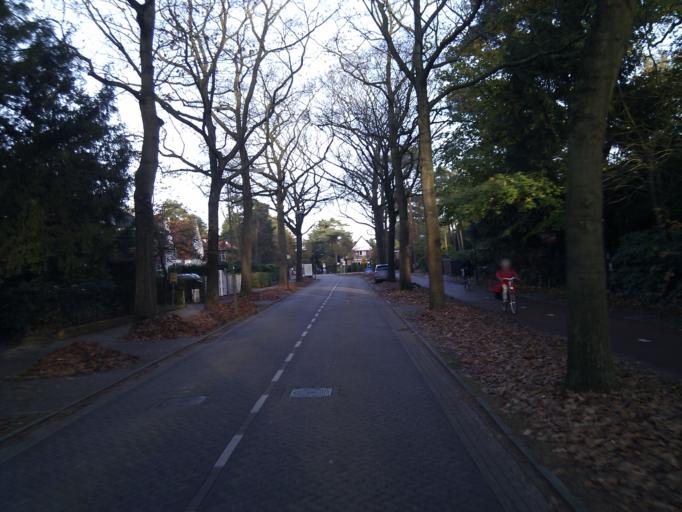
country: NL
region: Utrecht
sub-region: Gemeente De Bilt
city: De Bilt
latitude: 52.1329
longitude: 5.2176
